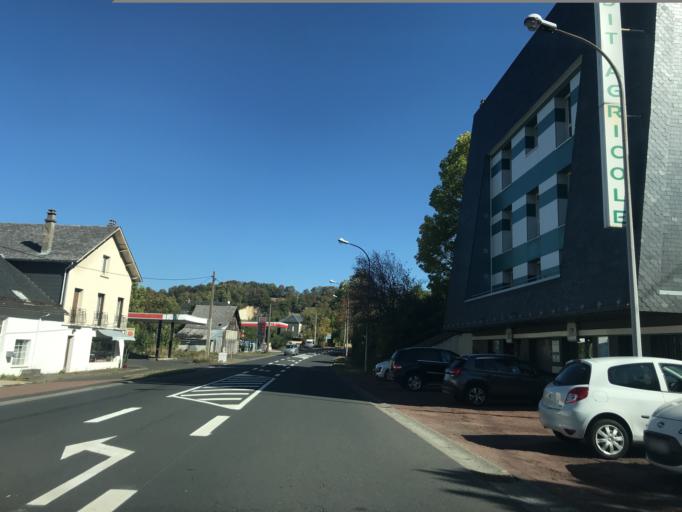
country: FR
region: Auvergne
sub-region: Departement du Puy-de-Dome
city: Gelles
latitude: 45.6869
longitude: 2.8052
